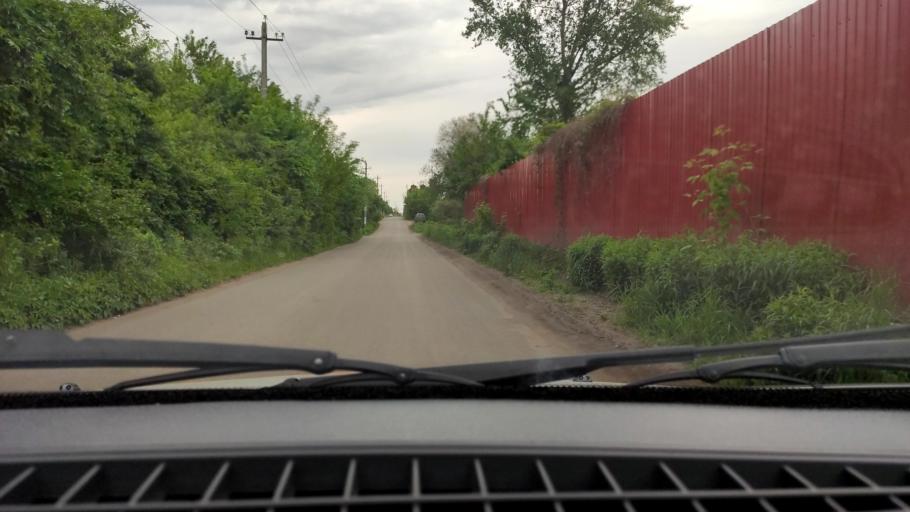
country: RU
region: Voronezj
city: Shilovo
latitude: 51.6022
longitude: 39.1401
